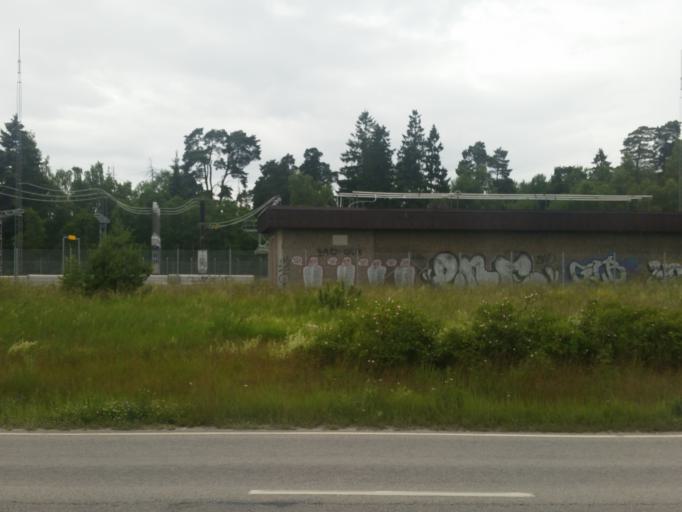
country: SE
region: Stockholm
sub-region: Stockholms Kommun
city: Kista
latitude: 59.4151
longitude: 17.9041
